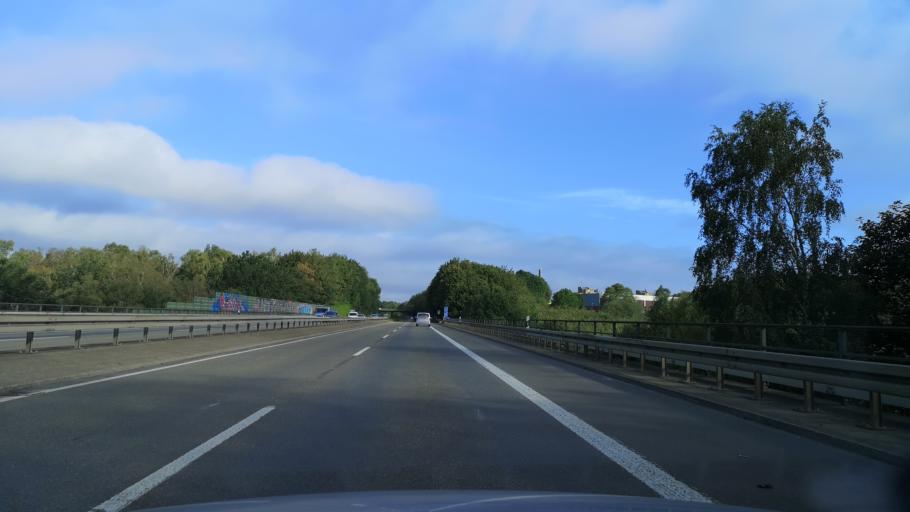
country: DE
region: North Rhine-Westphalia
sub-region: Regierungsbezirk Dusseldorf
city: Velbert
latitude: 51.3342
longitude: 7.0640
